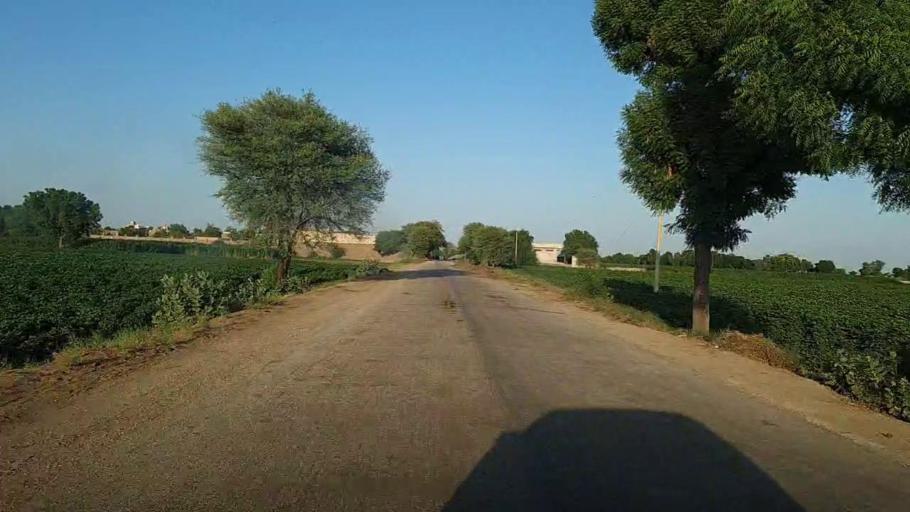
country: PK
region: Sindh
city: Bhan
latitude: 26.5835
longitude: 67.7677
